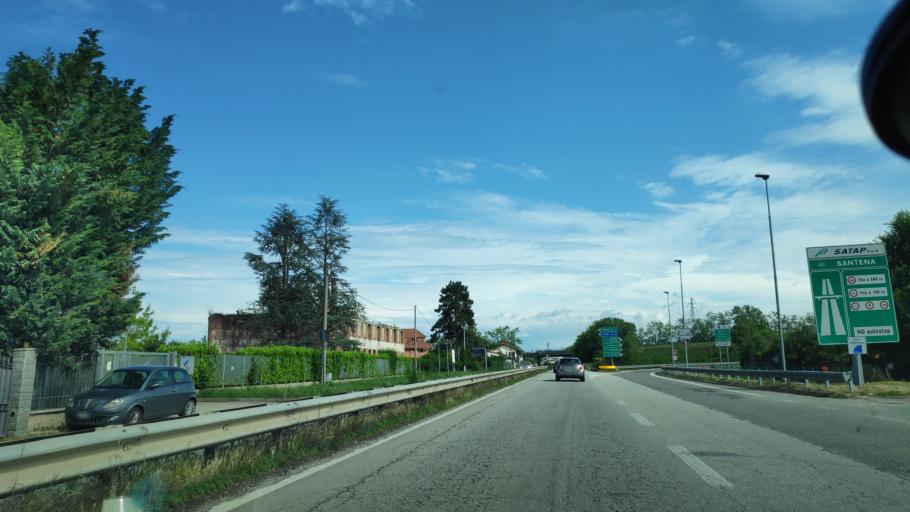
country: IT
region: Piedmont
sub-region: Provincia di Torino
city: Cambiano
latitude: 44.9621
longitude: 7.7790
